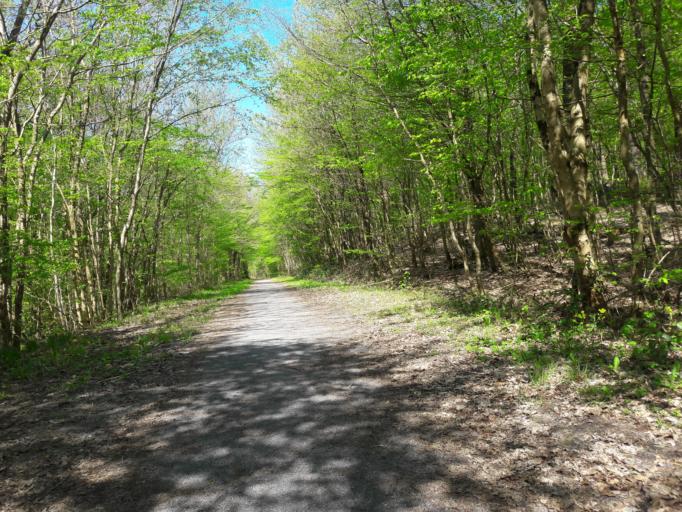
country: FR
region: Nord-Pas-de-Calais
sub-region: Departement du Nord
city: Sains-du-Nord
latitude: 50.1294
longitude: 4.0658
